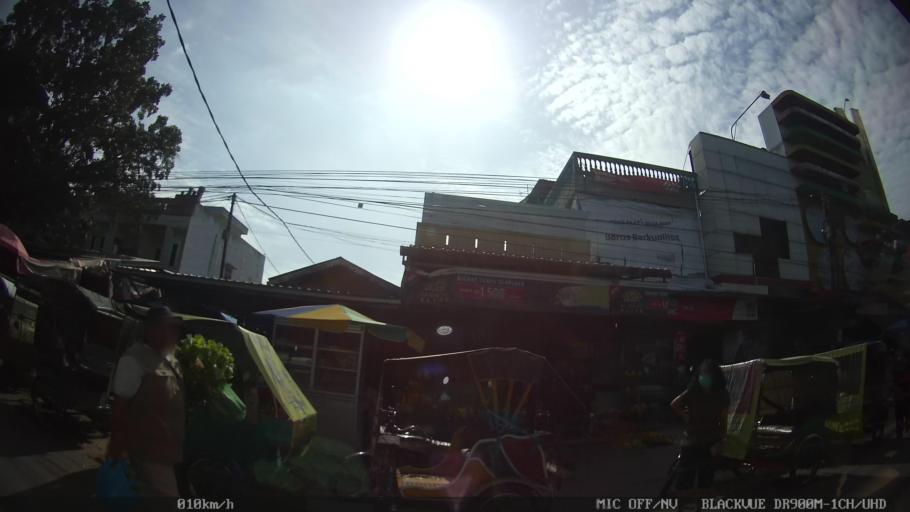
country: ID
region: North Sumatra
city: Medan
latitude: 3.5710
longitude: 98.6427
